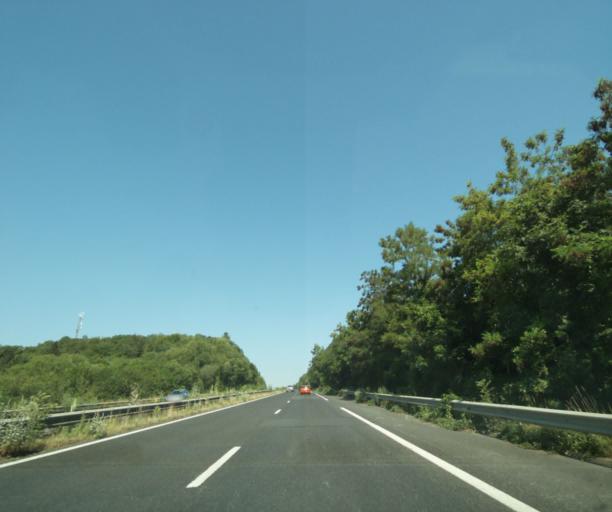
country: FR
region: Lorraine
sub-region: Departement de Meurthe-et-Moselle
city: Foug
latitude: 48.6729
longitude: 5.7748
